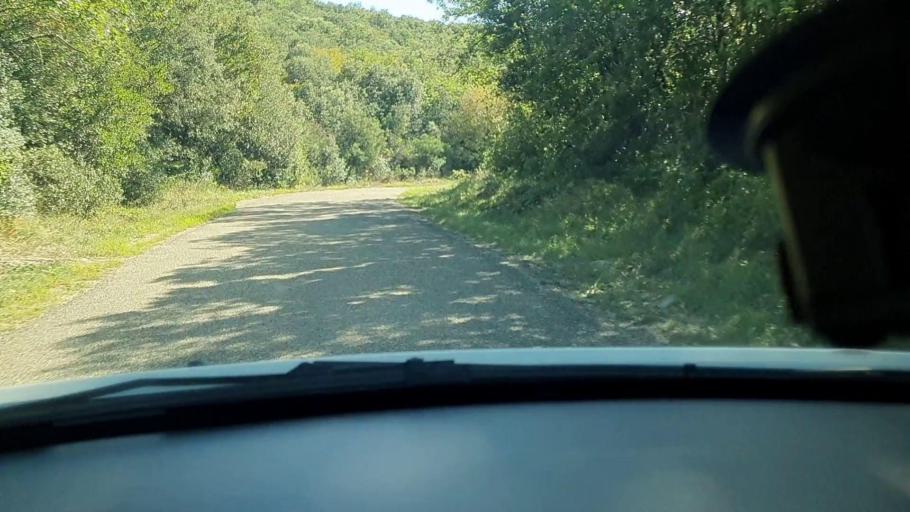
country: FR
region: Languedoc-Roussillon
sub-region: Departement du Gard
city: Goudargues
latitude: 44.1563
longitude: 4.4212
